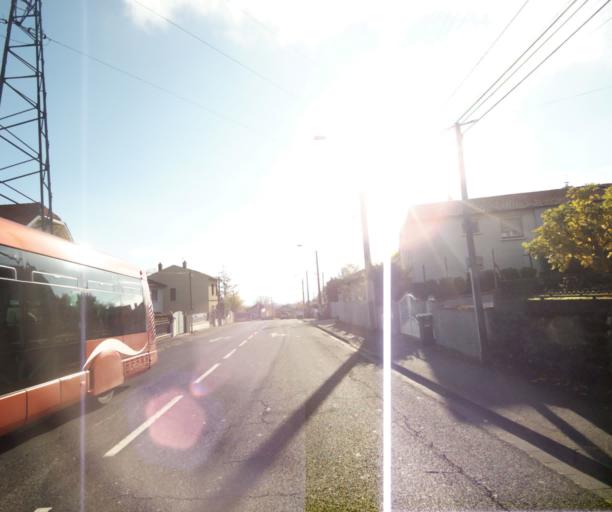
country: FR
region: Auvergne
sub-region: Departement du Puy-de-Dome
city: Aubiere
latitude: 45.7674
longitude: 3.1196
